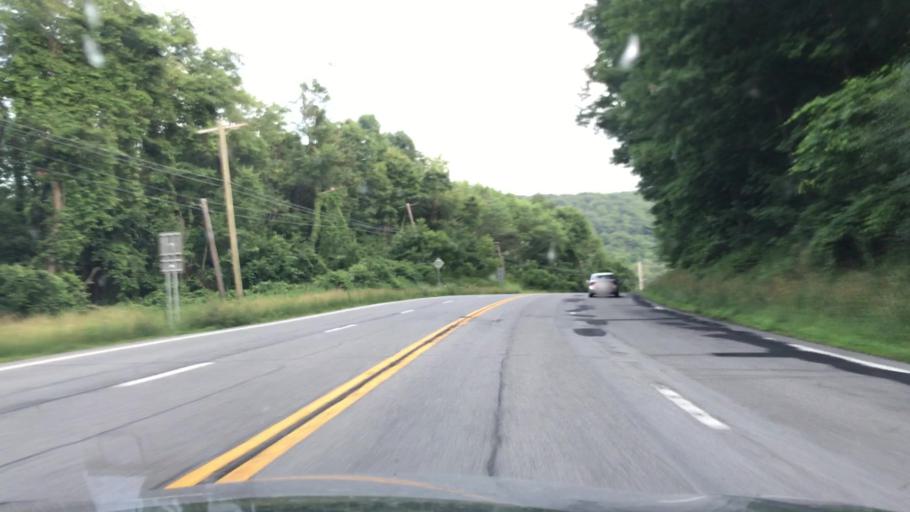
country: US
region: New York
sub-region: Orange County
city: Harriman
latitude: 41.2923
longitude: -74.1420
